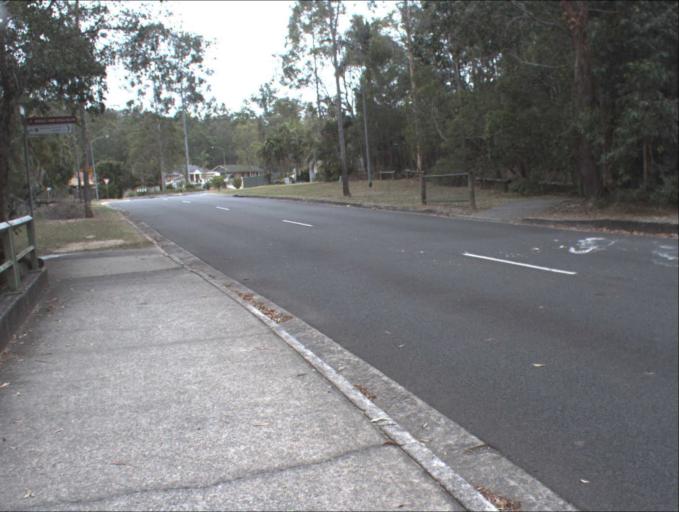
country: AU
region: Queensland
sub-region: Logan
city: Slacks Creek
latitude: -27.6567
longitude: 153.2011
